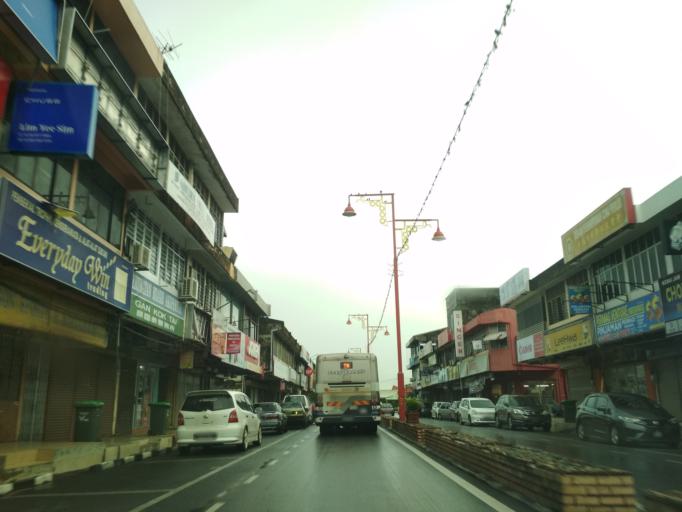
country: MY
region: Perlis
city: Kangar
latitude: 6.4356
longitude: 100.1914
